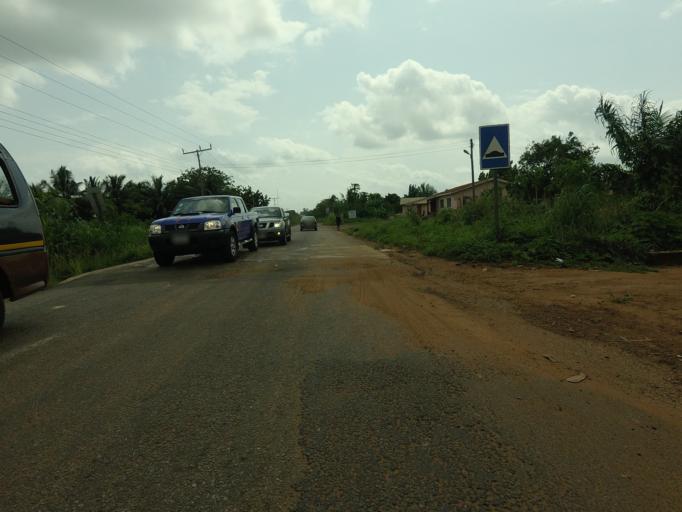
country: TG
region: Maritime
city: Lome
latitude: 6.2236
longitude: 1.0304
